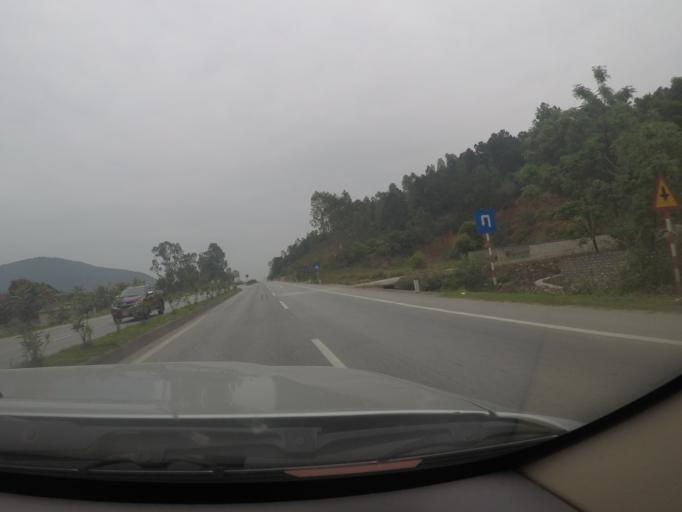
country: VN
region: Nghe An
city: Quan Hanh
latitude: 18.8626
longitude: 105.6394
